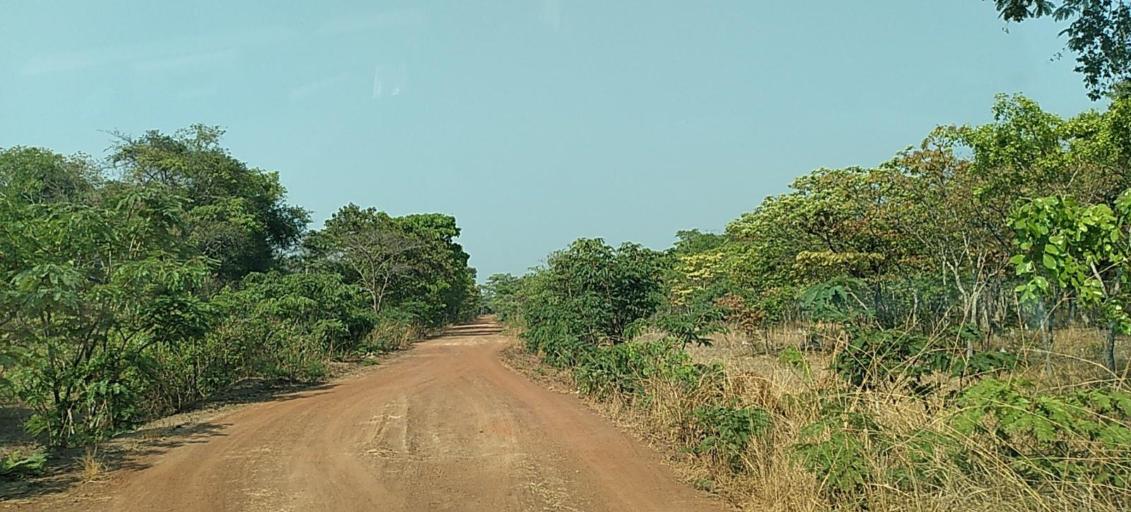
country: ZM
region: Copperbelt
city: Chingola
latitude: -12.8758
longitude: 27.4474
